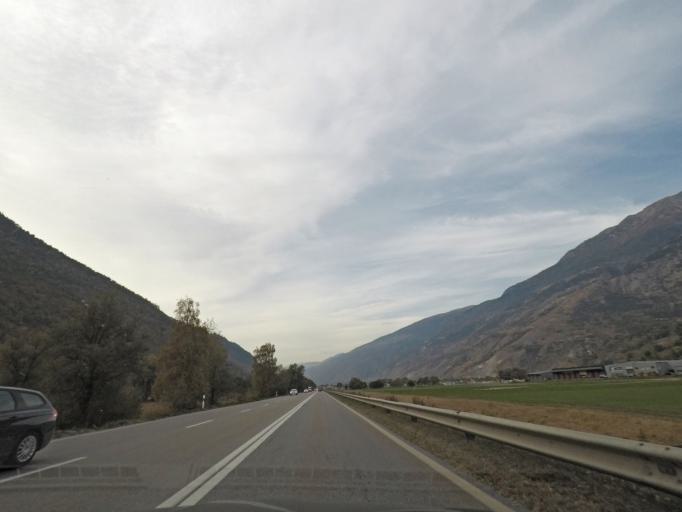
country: CH
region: Valais
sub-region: Raron District
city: Raron
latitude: 46.3014
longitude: 7.8148
